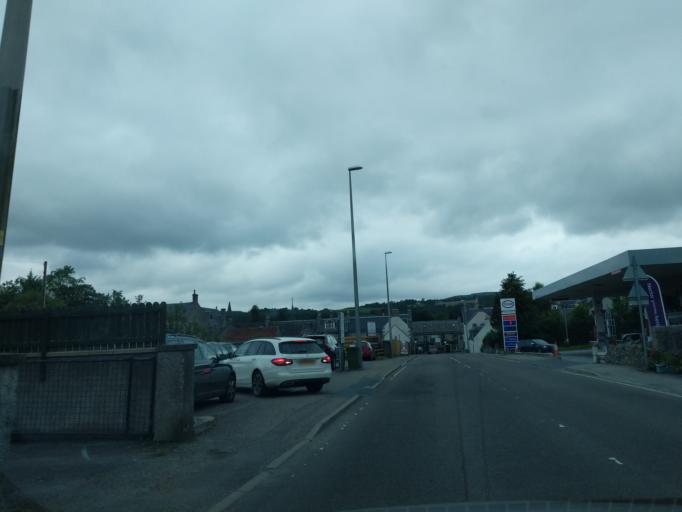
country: GB
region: Scotland
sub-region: Highland
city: Grantown on Spey
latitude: 57.3287
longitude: -3.6084
